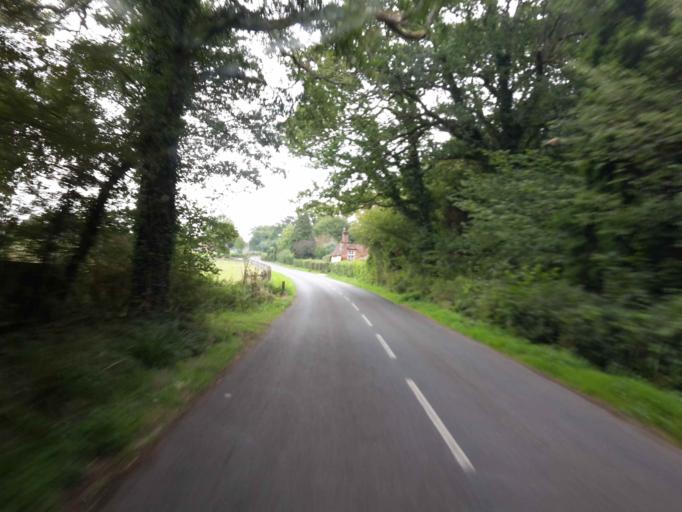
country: GB
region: England
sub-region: West Sussex
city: Rudgwick
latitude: 51.0618
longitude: -0.4444
